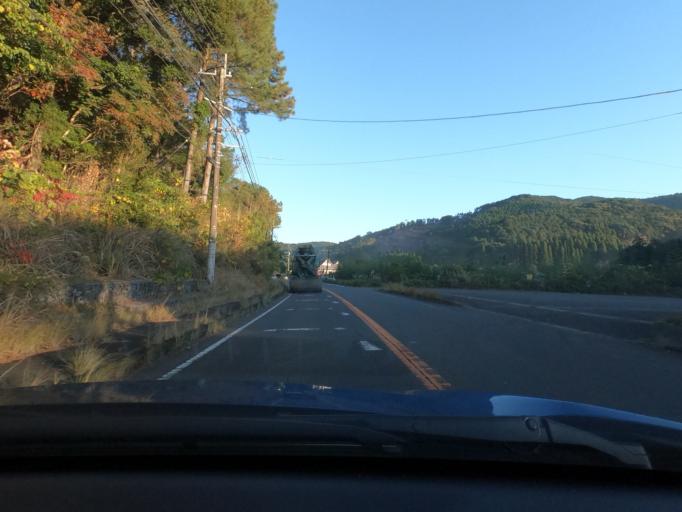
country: JP
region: Kagoshima
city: Satsumasendai
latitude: 31.8044
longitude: 130.3555
